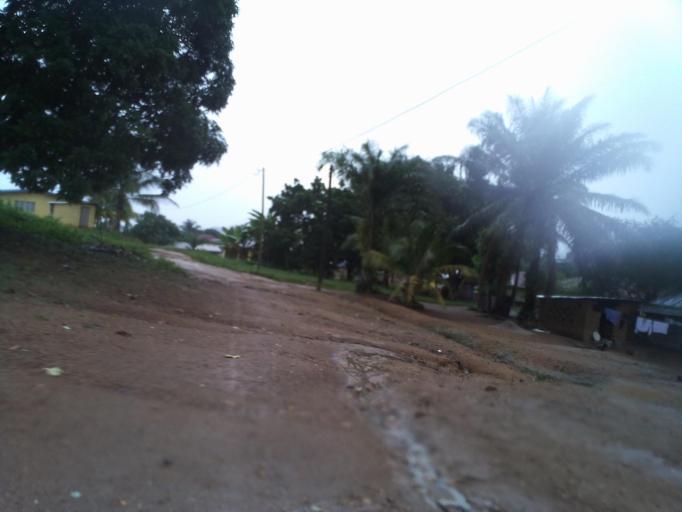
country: SL
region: Eastern Province
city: Kenema
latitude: 7.8543
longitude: -11.1918
